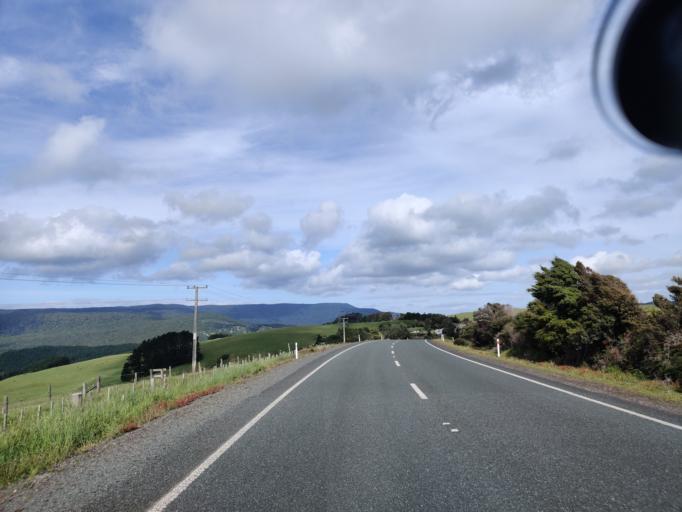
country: NZ
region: Northland
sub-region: Kaipara District
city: Dargaville
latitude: -35.7606
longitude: 173.6609
